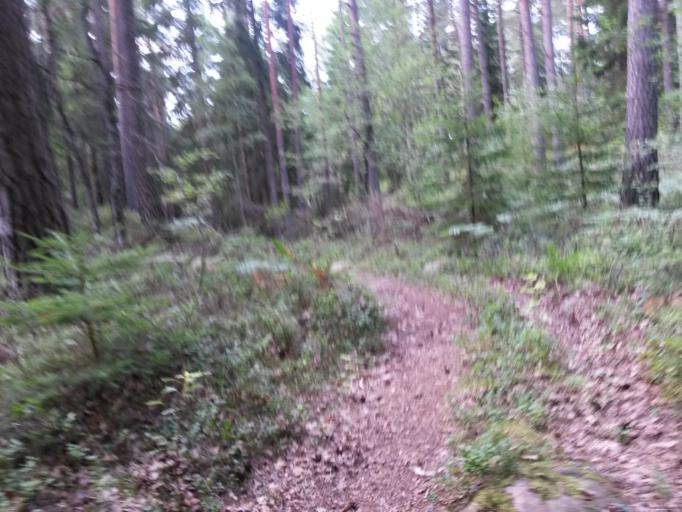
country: SE
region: Vaestra Goetaland
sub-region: Vargarda Kommun
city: Jonstorp
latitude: 57.9495
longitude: 12.6767
